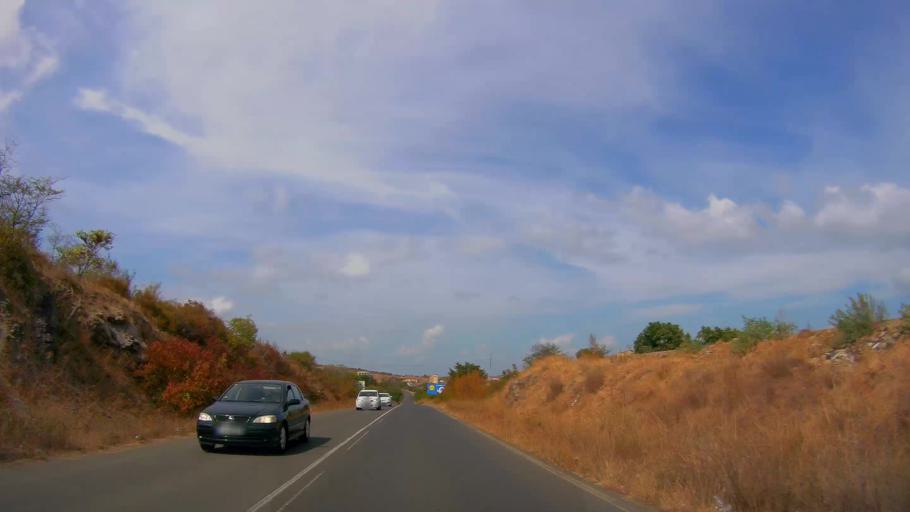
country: BG
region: Burgas
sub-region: Obshtina Sozopol
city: Sozopol
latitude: 42.4075
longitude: 27.7015
